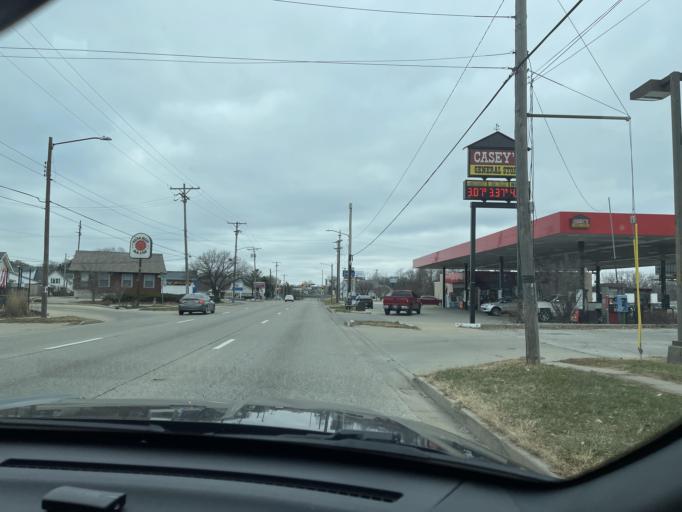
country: US
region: Illinois
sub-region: Sangamon County
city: Springfield
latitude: 39.8053
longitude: -89.6711
